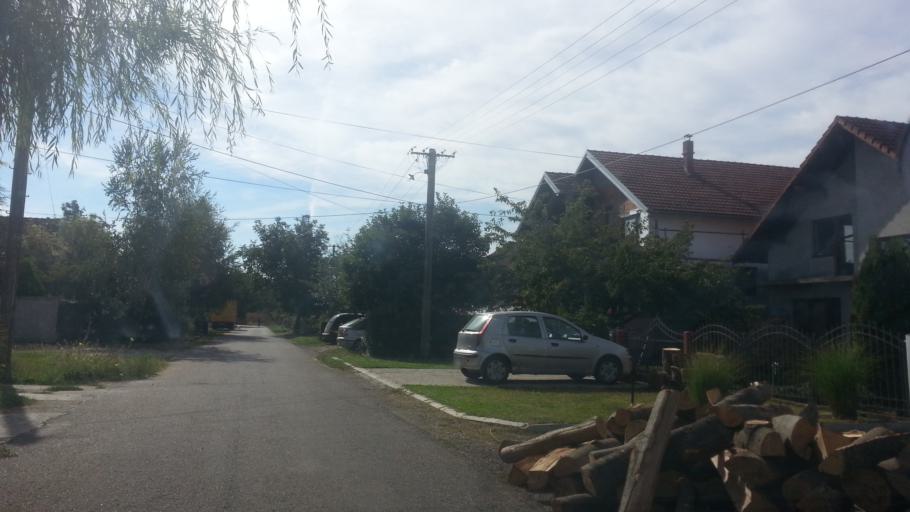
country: RS
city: Novi Banovci
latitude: 44.9687
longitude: 20.2752
